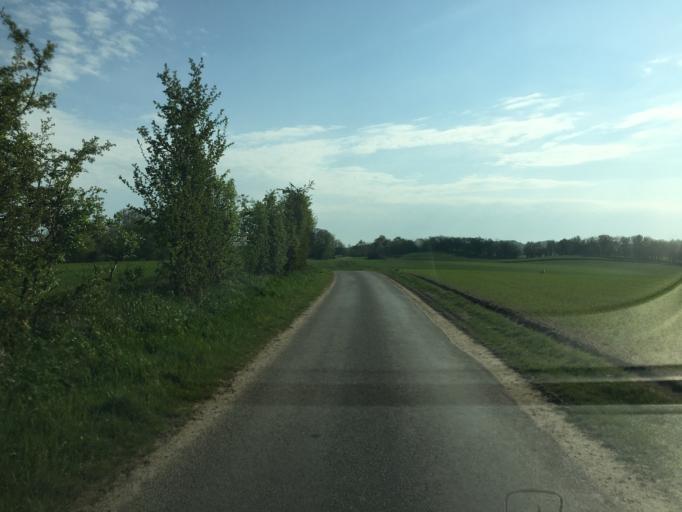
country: DK
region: South Denmark
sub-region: Aabenraa Kommune
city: Rodekro
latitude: 55.1470
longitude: 9.3794
